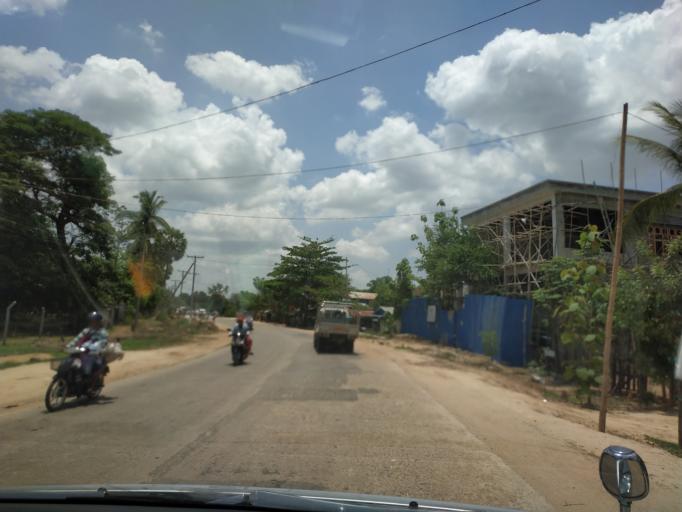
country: MM
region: Bago
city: Bago
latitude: 17.4757
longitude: 96.5177
